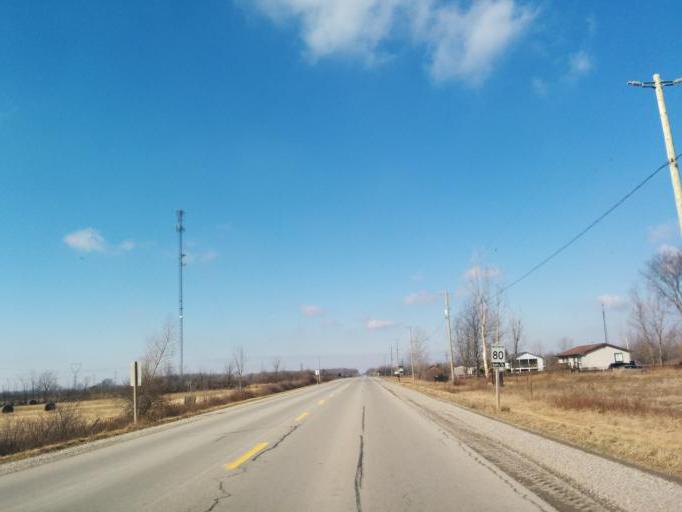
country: CA
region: Ontario
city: Brantford
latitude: 43.0071
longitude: -80.1741
